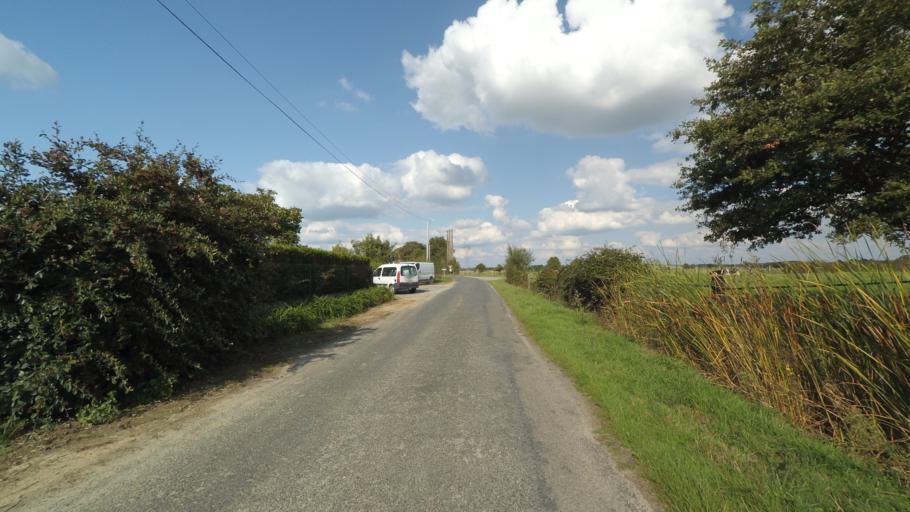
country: FR
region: Pays de la Loire
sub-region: Departement de la Loire-Atlantique
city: Vieillevigne
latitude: 46.9772
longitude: -1.4094
